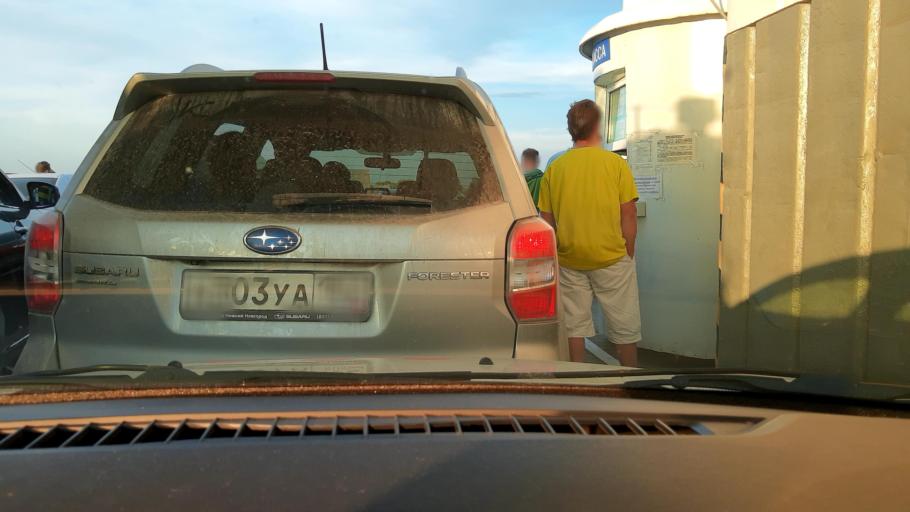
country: RU
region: Nizjnij Novgorod
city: Nizhniy Novgorod
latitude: 56.3381
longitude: 44.0325
